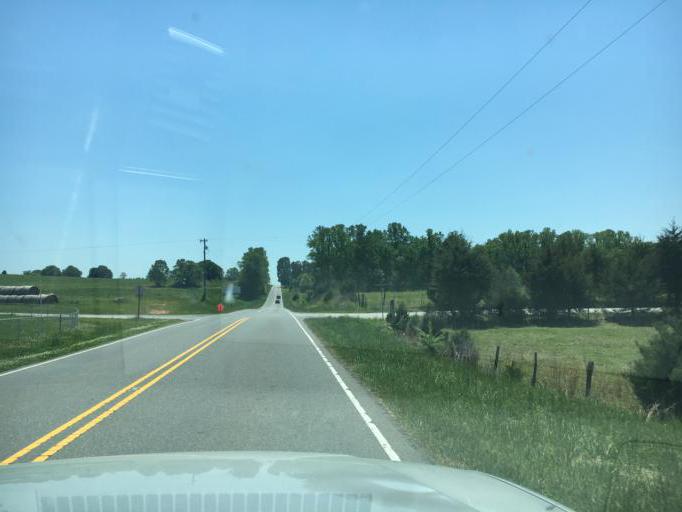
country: US
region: South Carolina
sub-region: Cherokee County
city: Blacksburg
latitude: 35.1813
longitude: -81.5712
